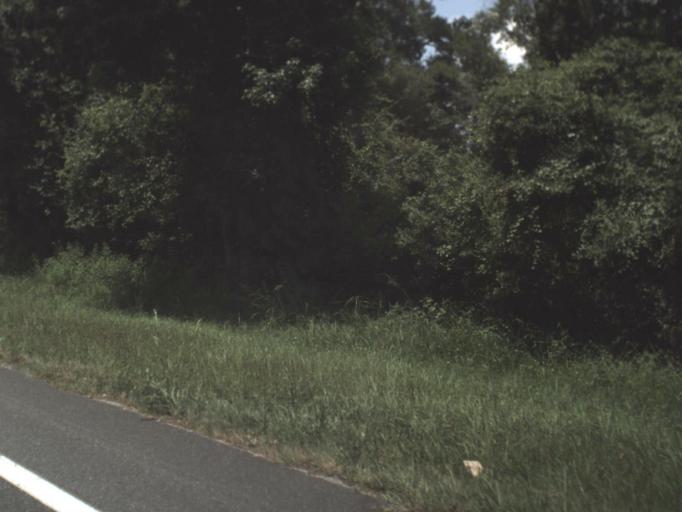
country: US
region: Florida
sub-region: Columbia County
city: Five Points
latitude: 30.2222
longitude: -82.6585
